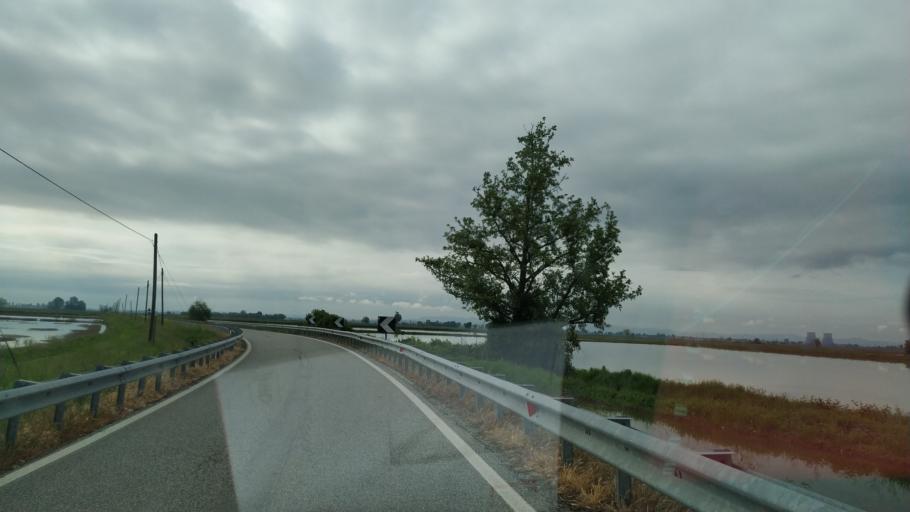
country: IT
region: Piedmont
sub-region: Provincia di Vercelli
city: Crova
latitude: 45.3099
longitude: 8.2023
